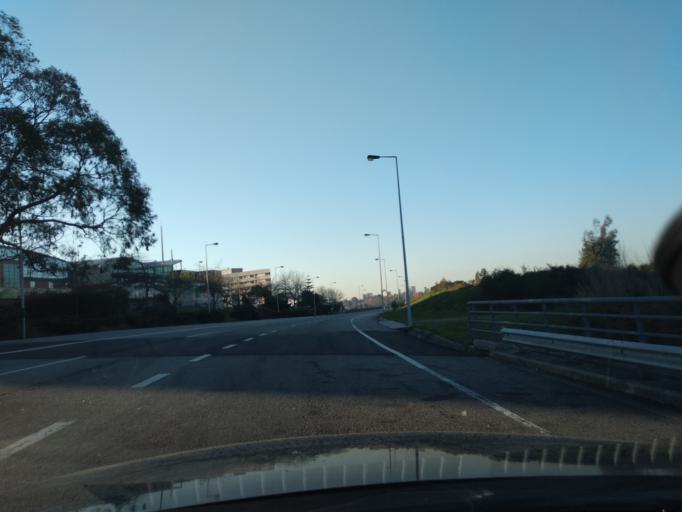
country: PT
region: Porto
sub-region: Vila Nova de Gaia
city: Vila Nova de Gaia
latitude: 41.1409
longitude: -8.6342
